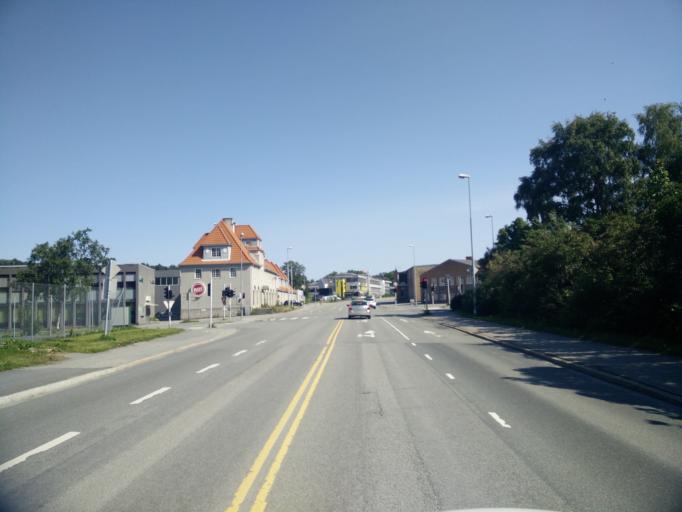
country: NO
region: Sor-Trondelag
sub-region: Trondheim
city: Trondheim
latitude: 63.4411
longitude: 10.4321
